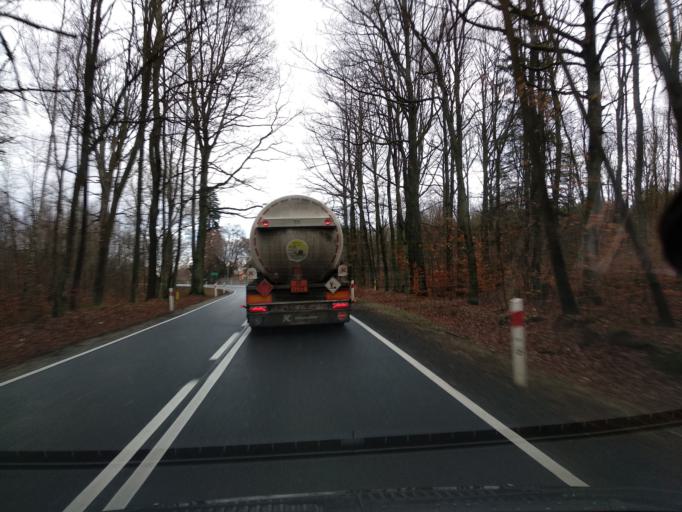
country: PL
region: Lower Silesian Voivodeship
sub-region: Powiat olesnicki
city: Twardogora
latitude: 51.3259
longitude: 17.5751
